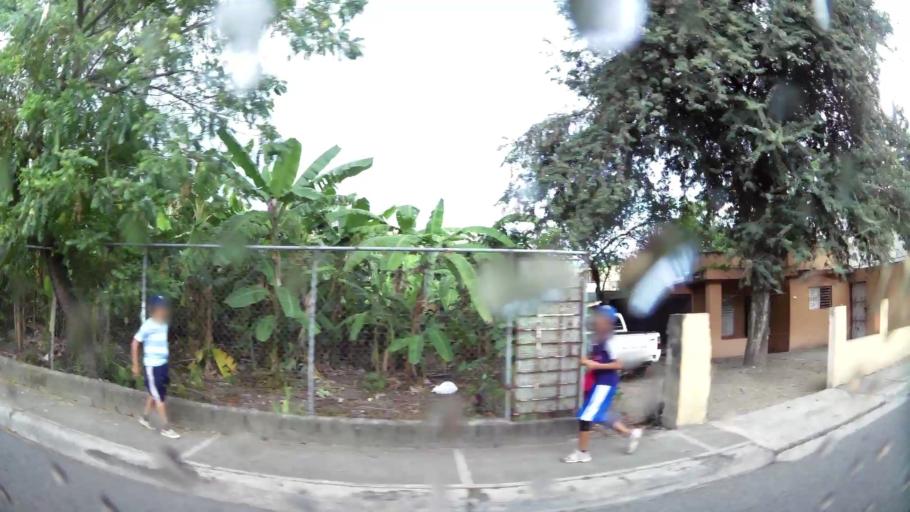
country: DO
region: Monsenor Nouel
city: Bonao
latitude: 18.9301
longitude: -70.4056
